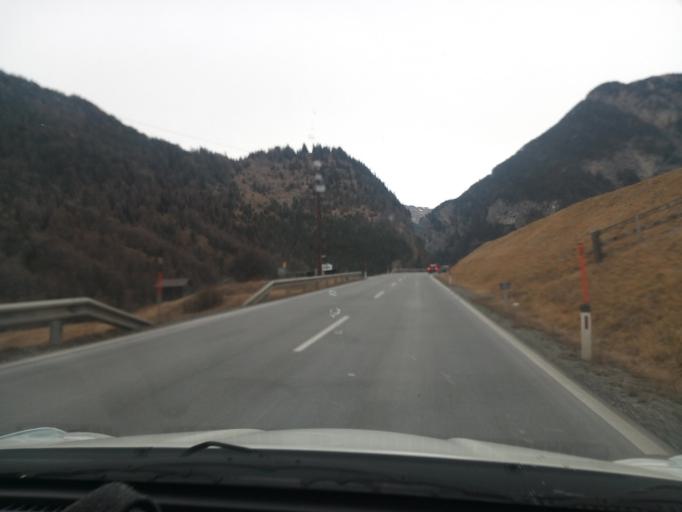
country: AT
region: Tyrol
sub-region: Politischer Bezirk Landeck
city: Nauders
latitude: 46.8998
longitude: 10.4953
